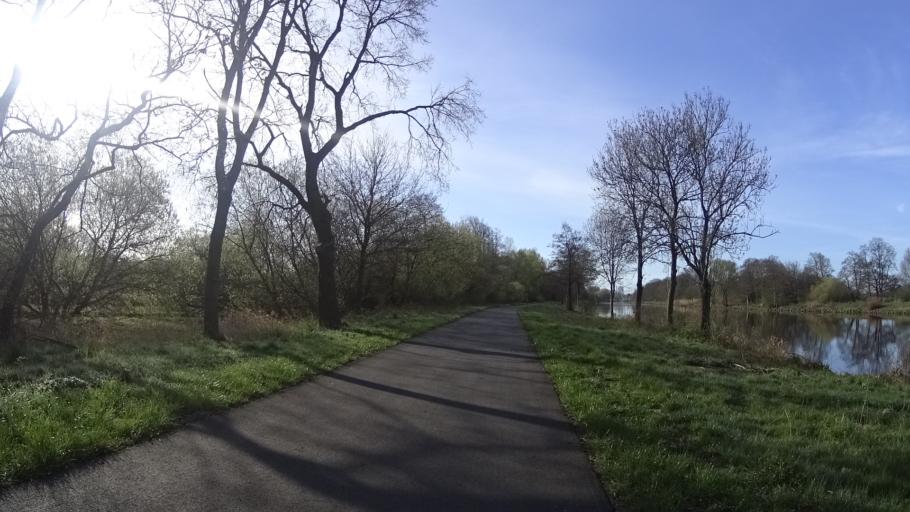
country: DE
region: Lower Saxony
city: Haren
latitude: 52.8056
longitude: 7.2594
